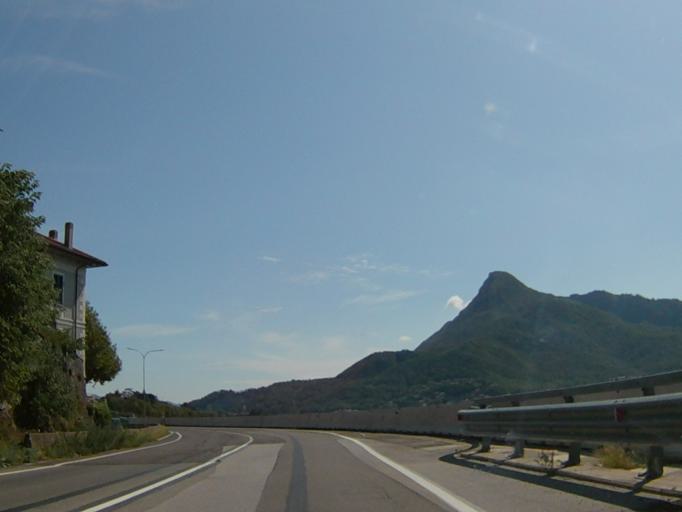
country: IT
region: Lombardy
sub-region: Provincia di Lecco
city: Lecco
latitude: 45.8684
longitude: 9.3784
